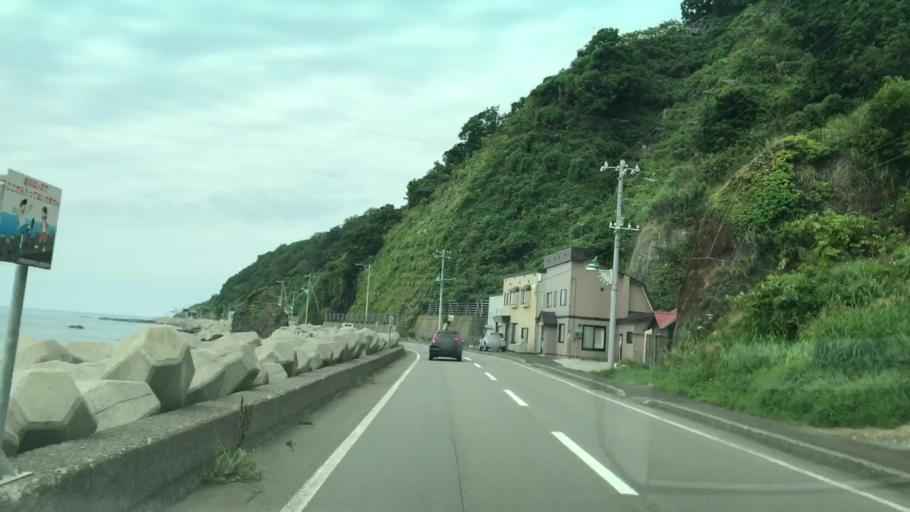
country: JP
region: Hokkaido
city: Iwanai
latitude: 43.1589
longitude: 140.4008
